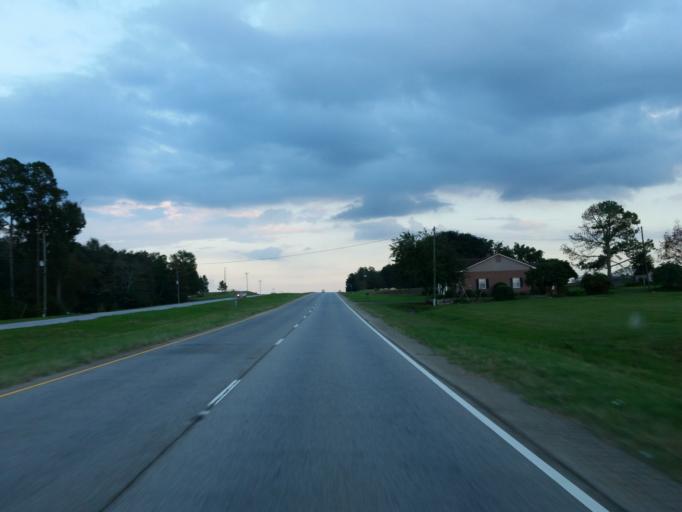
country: US
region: Georgia
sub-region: Pulaski County
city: Hawkinsville
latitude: 32.3217
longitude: -83.5494
